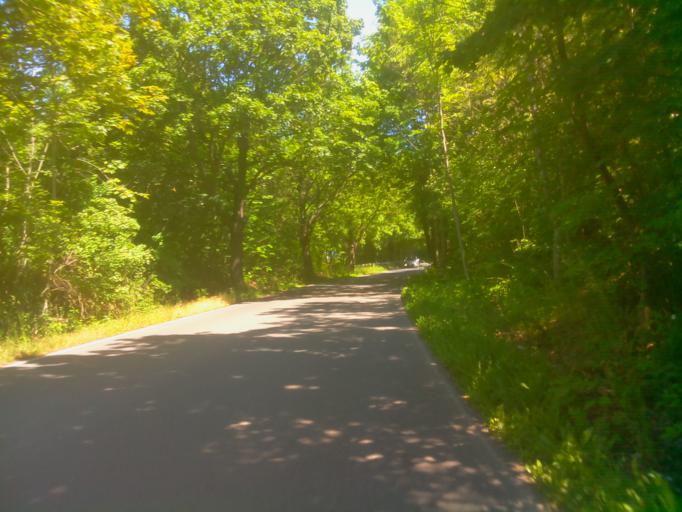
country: DE
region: Thuringia
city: Saalfeld
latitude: 50.6451
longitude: 11.3772
